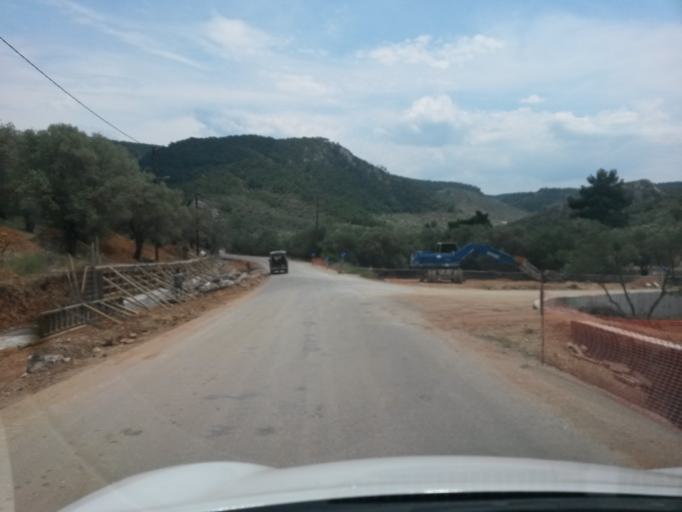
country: GR
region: North Aegean
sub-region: Nomos Lesvou
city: Pamfylla
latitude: 39.1789
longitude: 26.4217
